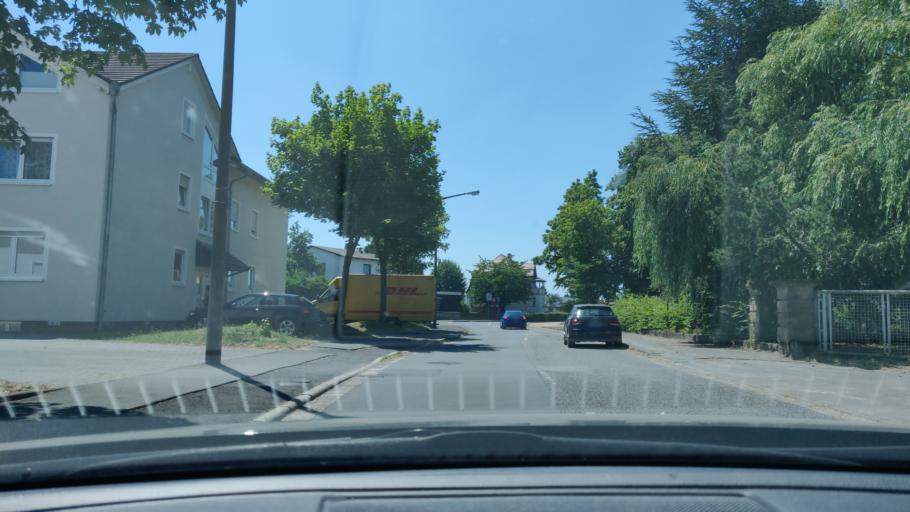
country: DE
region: Hesse
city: Fritzlar
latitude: 51.1375
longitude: 9.2755
